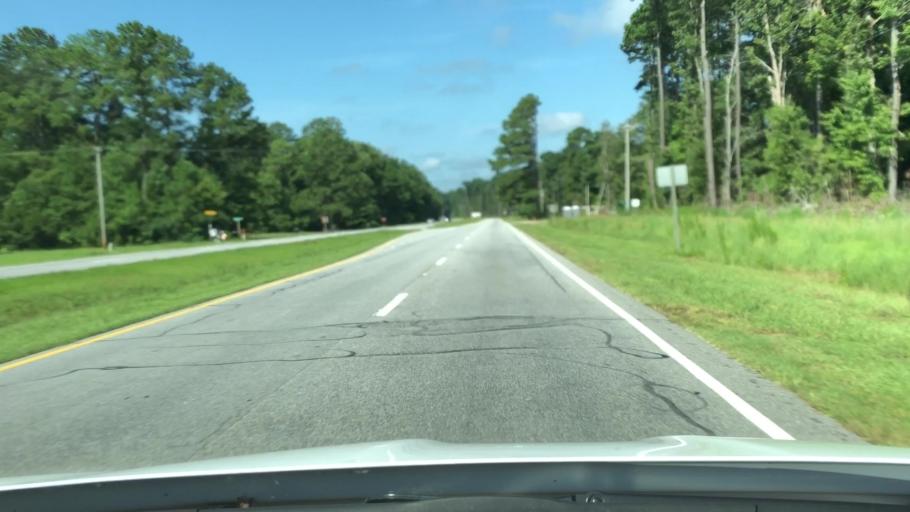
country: US
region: North Carolina
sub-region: Bertie County
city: Windsor
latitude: 35.9339
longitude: -76.9827
